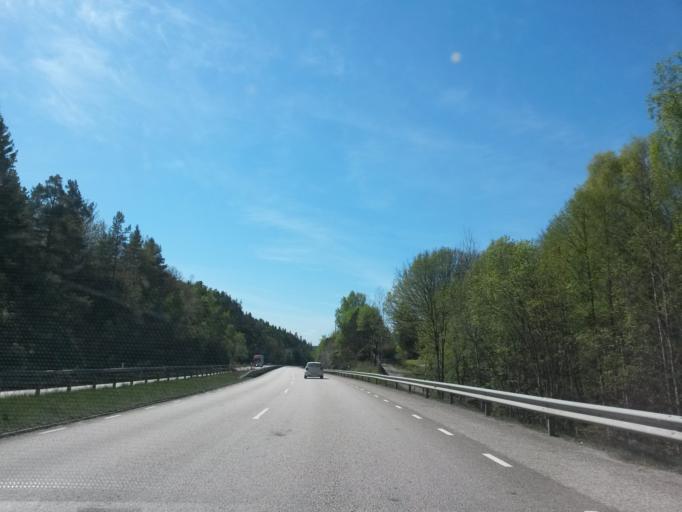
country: SE
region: Vaestra Goetaland
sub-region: Alingsas Kommun
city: Ingared
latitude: 57.8351
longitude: 12.4385
